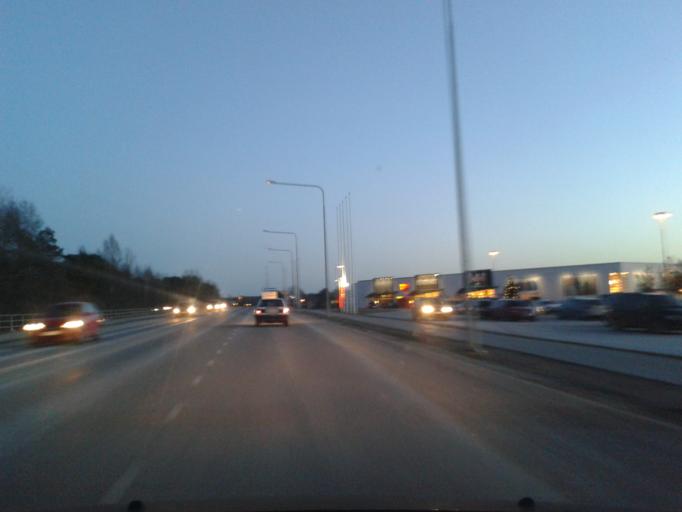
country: SE
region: Gotland
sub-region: Gotland
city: Visby
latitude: 57.6244
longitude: 18.3233
